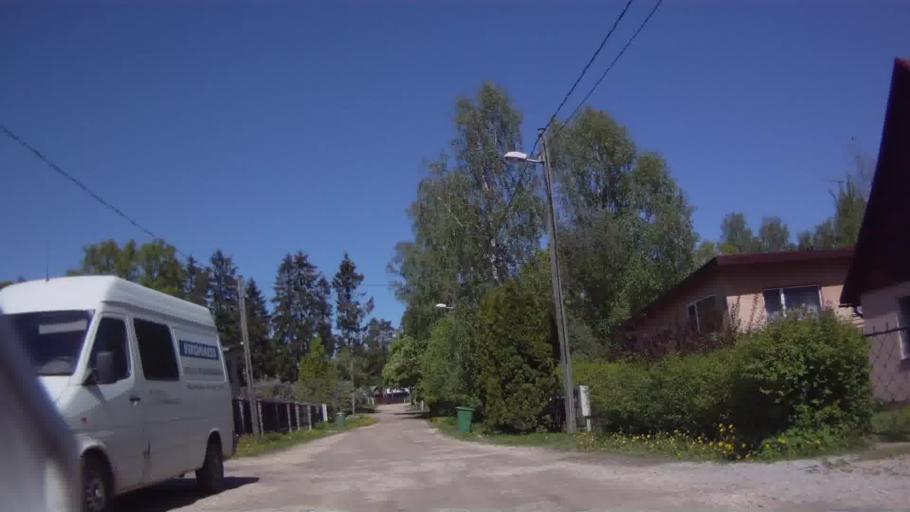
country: LV
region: Riga
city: Bergi
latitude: 56.9877
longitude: 24.2991
